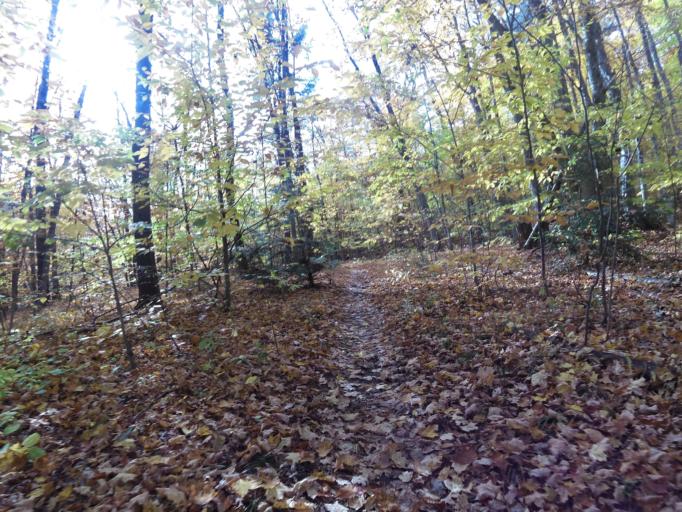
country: CA
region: Quebec
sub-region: Outaouais
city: Gatineau
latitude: 45.4838
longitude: -75.8155
